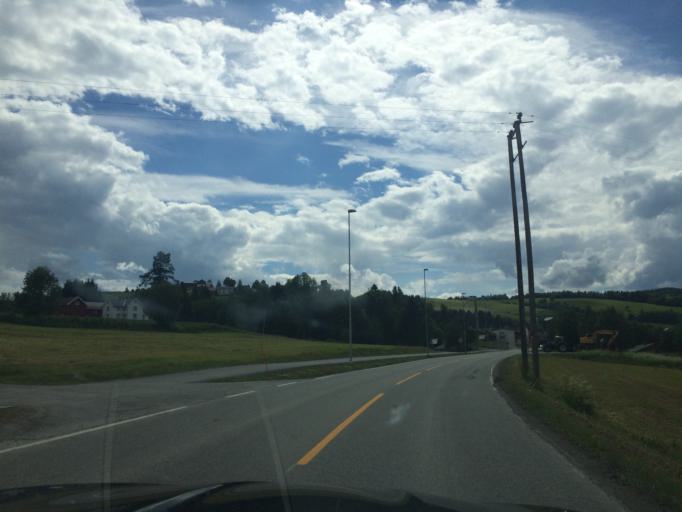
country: NO
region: Sor-Trondelag
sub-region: Selbu
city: Mebonden
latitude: 63.2451
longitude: 11.0907
